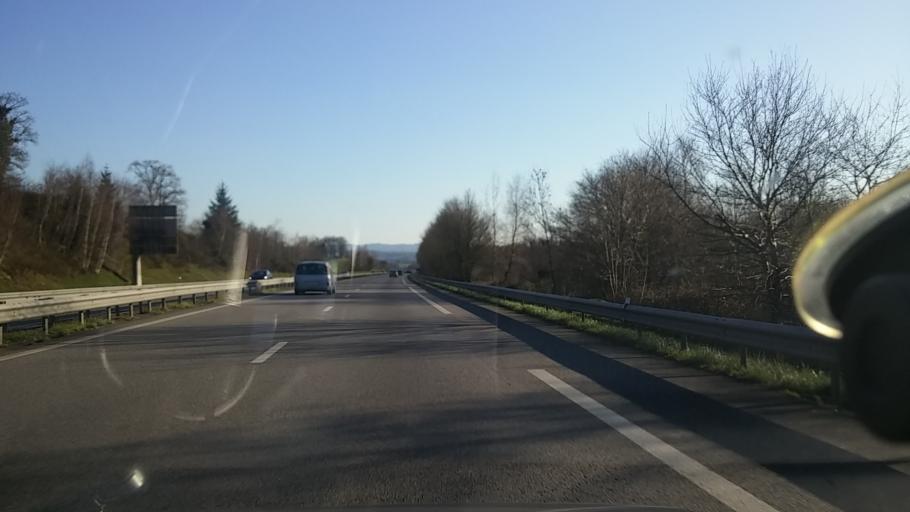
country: FR
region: Limousin
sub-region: Departement de la Creuse
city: Saint-Maurice-la-Souterraine
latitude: 46.1861
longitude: 1.3816
